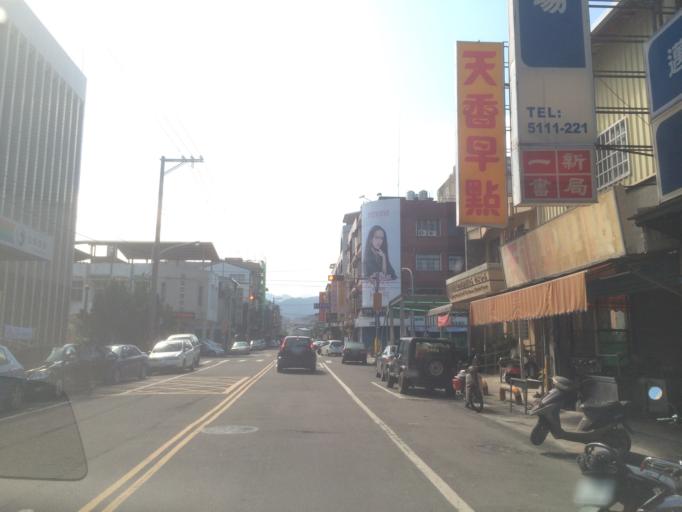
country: TW
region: Taiwan
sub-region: Hsinchu
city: Zhubei
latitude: 24.7363
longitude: 121.0919
